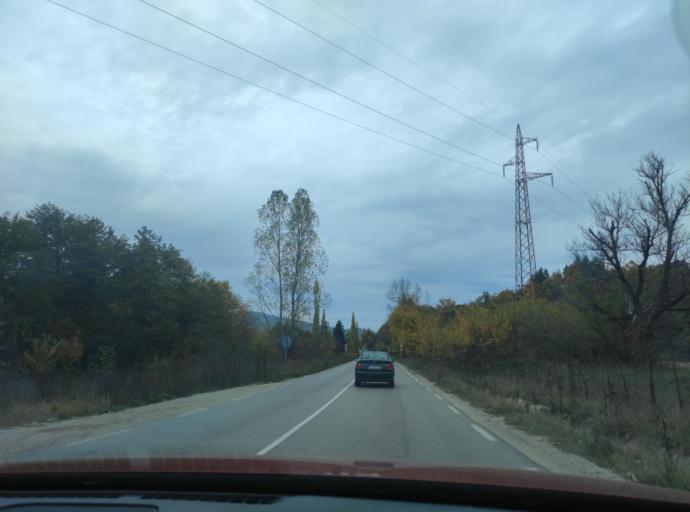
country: BG
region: Montana
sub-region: Obshtina Berkovitsa
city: Berkovitsa
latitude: 43.2626
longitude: 23.1784
